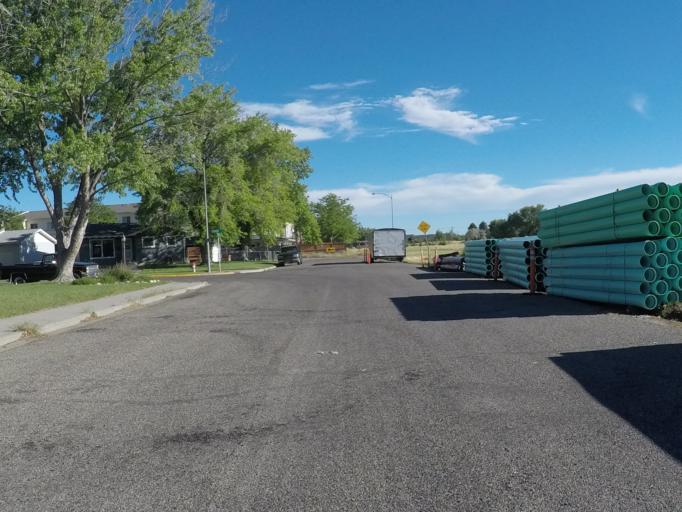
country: US
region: Montana
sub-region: Yellowstone County
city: Billings
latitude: 45.7732
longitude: -108.5861
